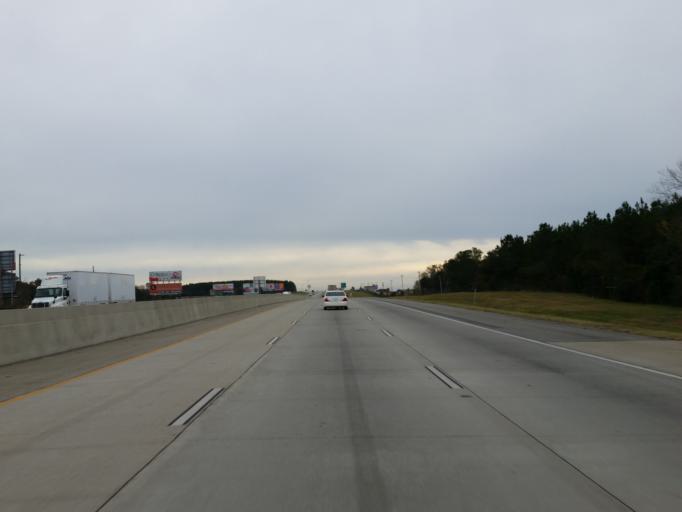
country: US
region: Georgia
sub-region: Crisp County
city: Cordele
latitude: 31.9516
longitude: -83.7503
